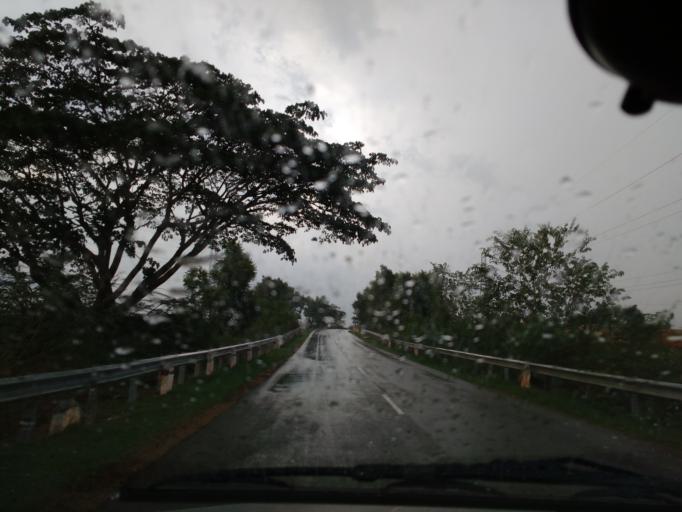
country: IN
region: Karnataka
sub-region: Tumkur
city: Tiptur
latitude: 13.2894
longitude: 76.5695
